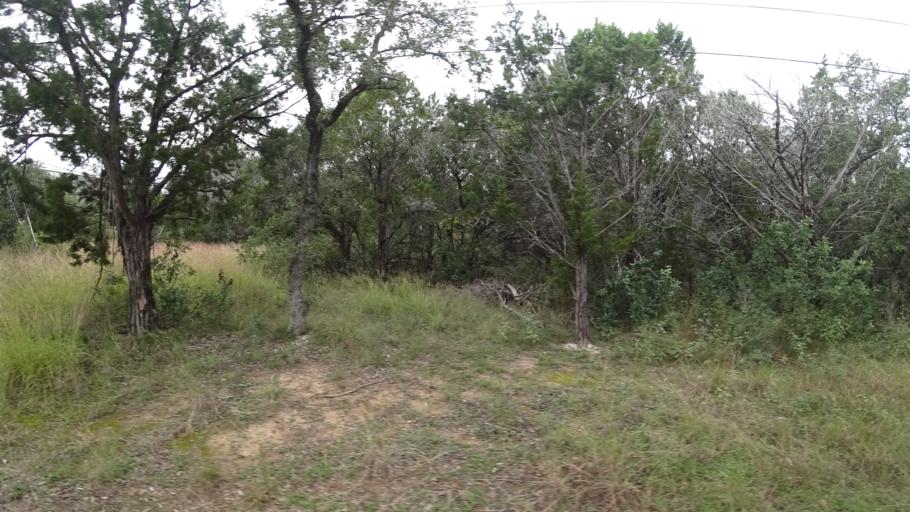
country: US
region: Texas
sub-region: Travis County
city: Hudson Bend
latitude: 30.3992
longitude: -97.9123
